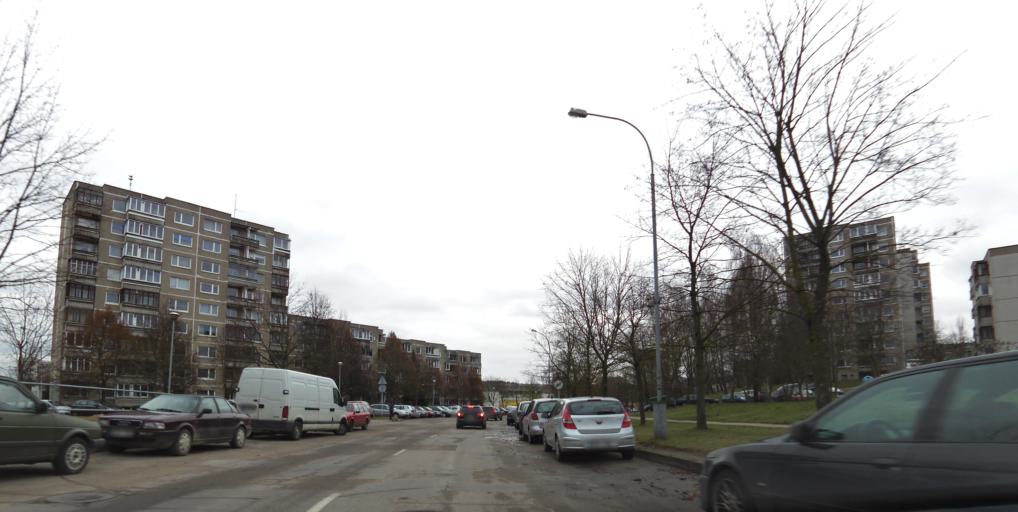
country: LT
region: Vilnius County
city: Justiniskes
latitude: 54.7205
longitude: 25.2283
